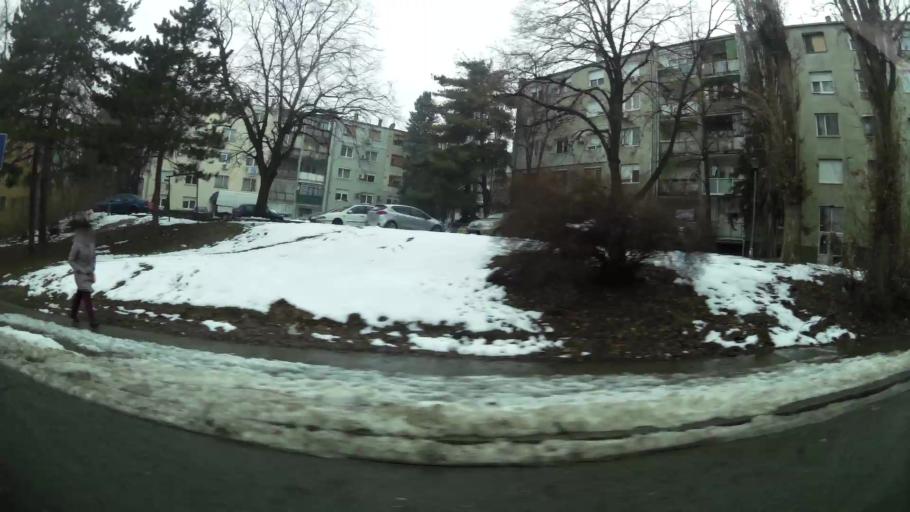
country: RS
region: Central Serbia
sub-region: Belgrade
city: Vozdovac
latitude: 44.7678
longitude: 20.4944
